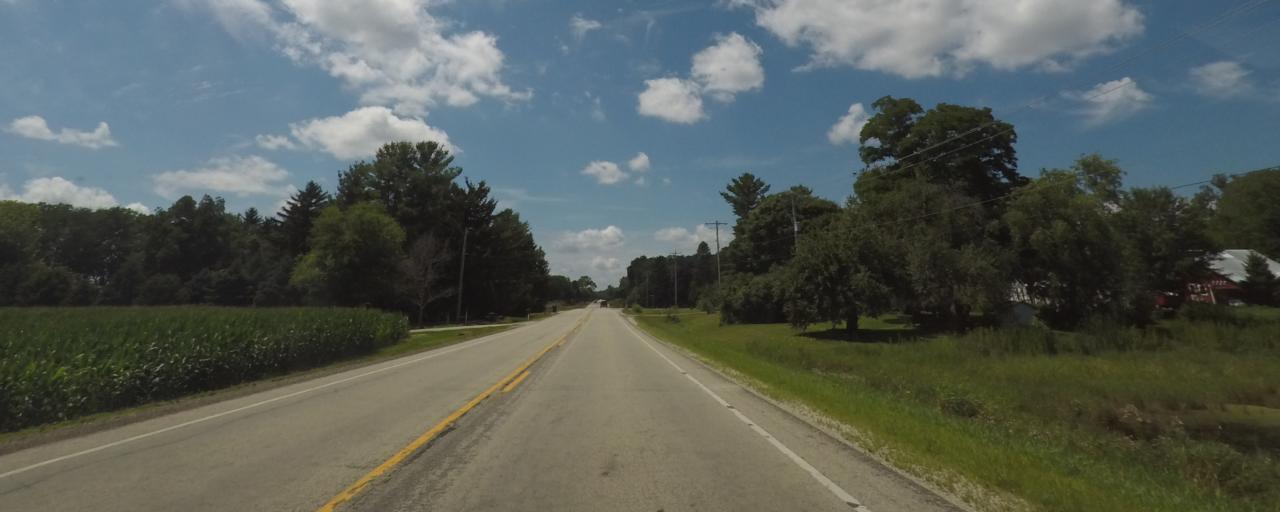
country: US
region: Wisconsin
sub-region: Jefferson County
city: Fort Atkinson
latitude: 42.9390
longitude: -88.7616
